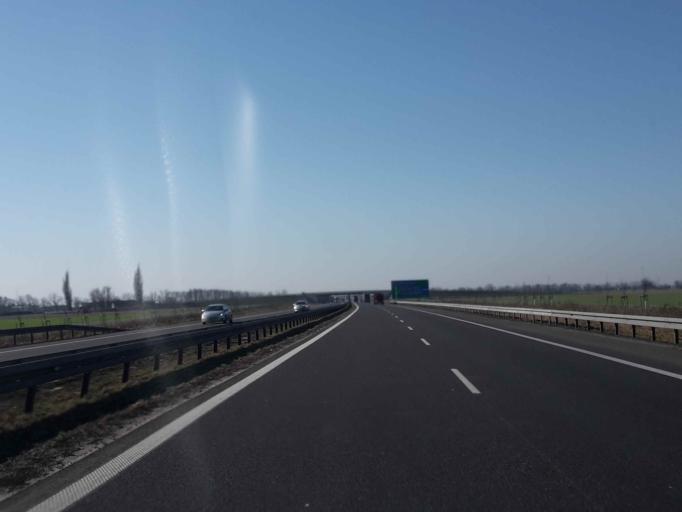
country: PL
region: Greater Poland Voivodeship
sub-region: Powiat poznanski
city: Kleszczewo
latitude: 52.3336
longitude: 17.1522
